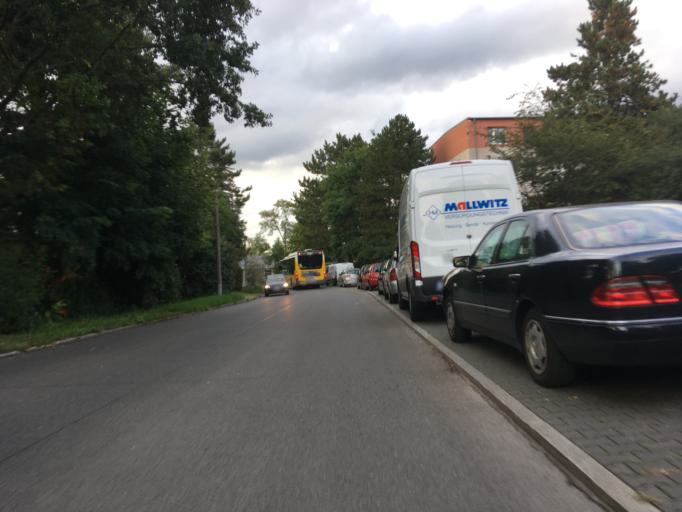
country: DE
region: Berlin
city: Johannisthal
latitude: 52.4407
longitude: 13.4947
